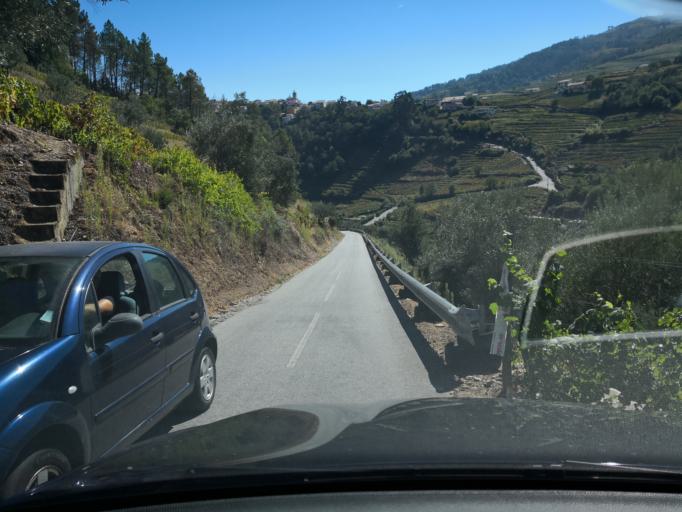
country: PT
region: Vila Real
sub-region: Santa Marta de Penaguiao
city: Santa Marta de Penaguiao
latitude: 41.2520
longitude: -7.8146
